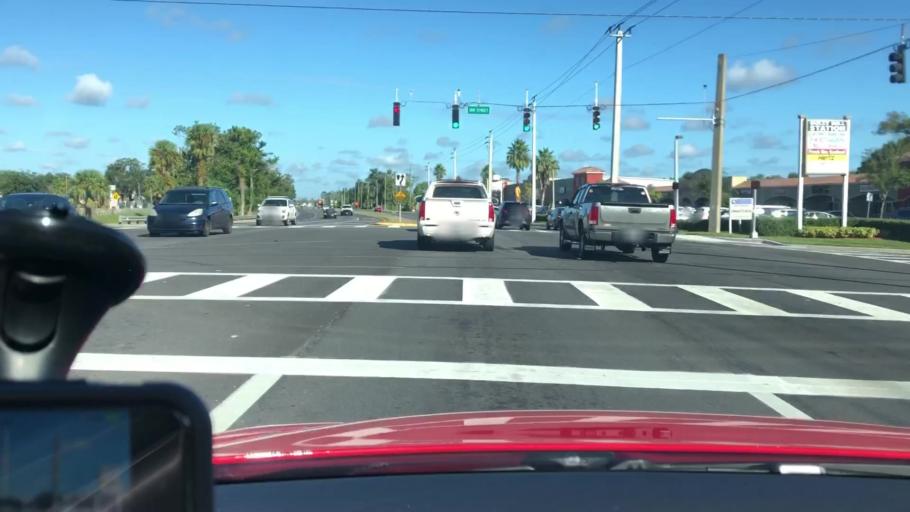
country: US
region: Florida
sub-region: Volusia County
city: Holly Hill
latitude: 29.2246
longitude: -81.0496
